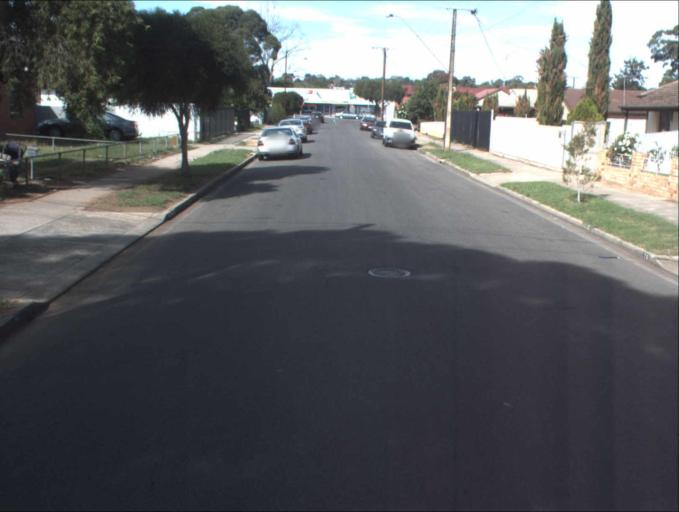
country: AU
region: South Australia
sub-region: Port Adelaide Enfield
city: Blair Athol
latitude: -34.8596
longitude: 138.5907
